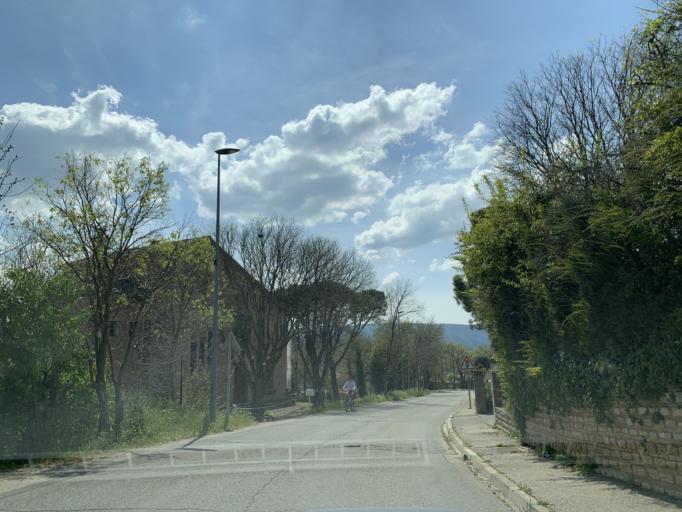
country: FR
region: Provence-Alpes-Cote d'Azur
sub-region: Departement du Vaucluse
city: Goult
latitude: 43.8616
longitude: 5.2465
